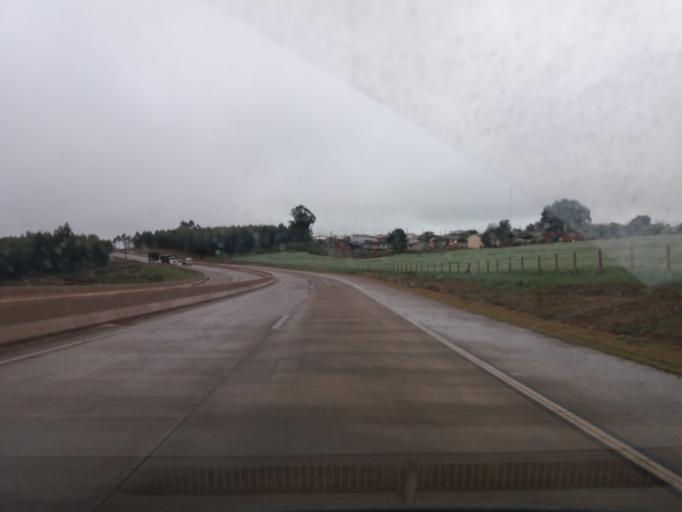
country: BR
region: Parana
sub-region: Cascavel
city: Cascavel
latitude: -25.1436
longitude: -53.5926
